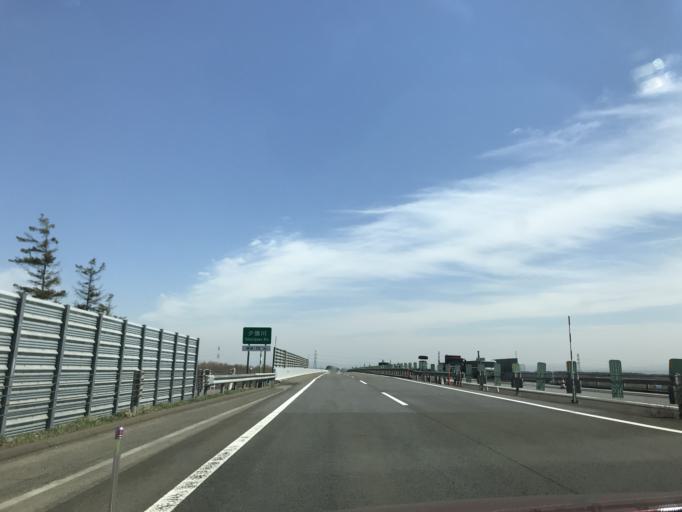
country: JP
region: Hokkaido
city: Ebetsu
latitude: 43.1133
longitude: 141.6155
